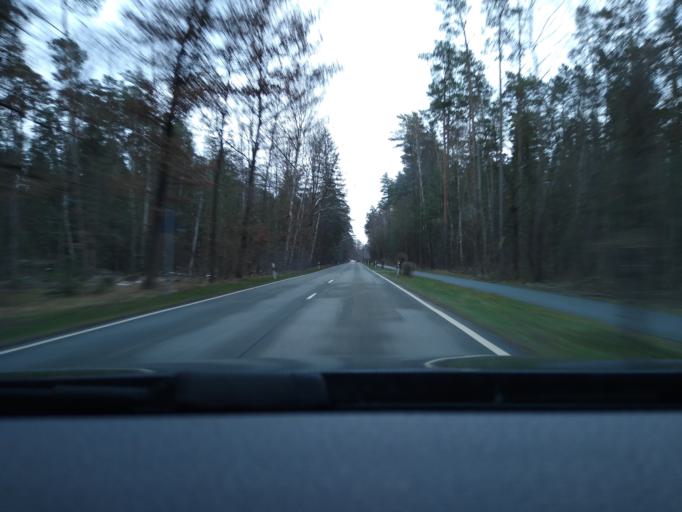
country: DE
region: Bavaria
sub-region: Regierungsbezirk Mittelfranken
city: Seukendorf
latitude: 49.4605
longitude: 10.9123
